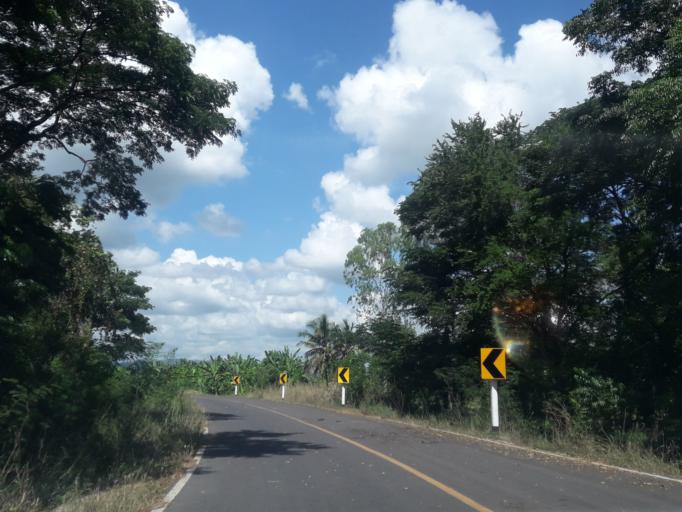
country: TH
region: Lop Buri
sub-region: Amphoe Tha Luang
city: Tha Luang
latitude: 15.0696
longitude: 101.0412
